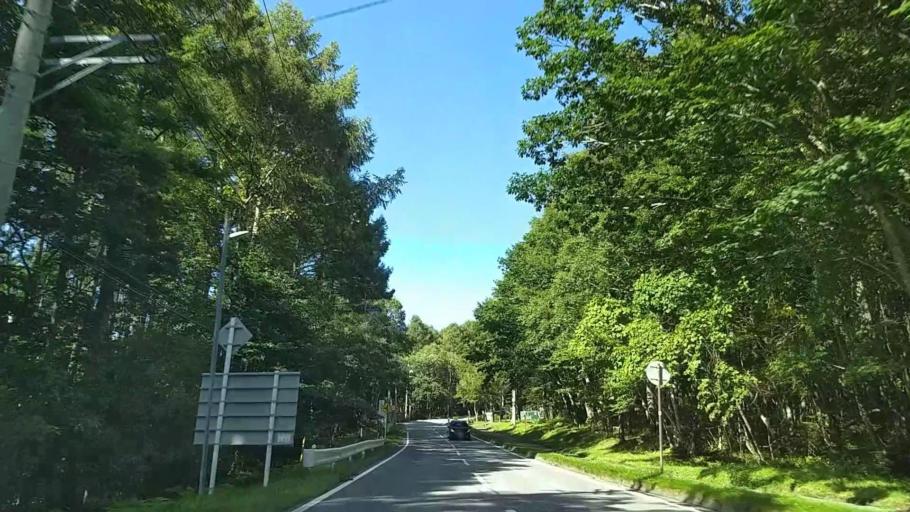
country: JP
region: Nagano
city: Chino
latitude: 36.1260
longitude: 138.2680
